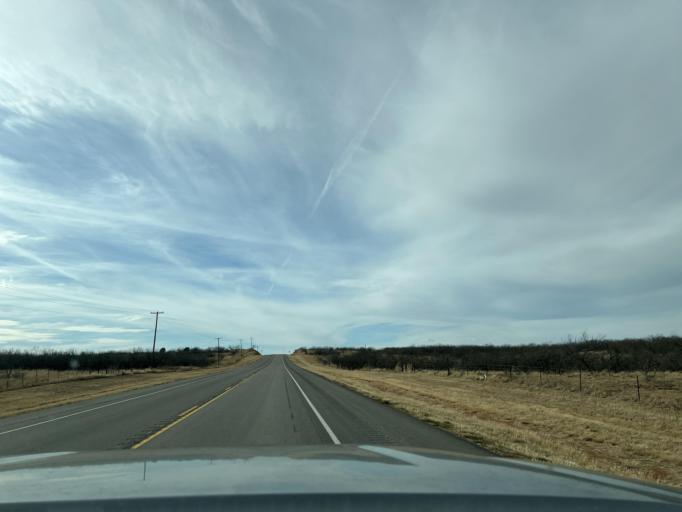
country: US
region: Texas
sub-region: Jones County
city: Anson
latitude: 32.7509
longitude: -99.7421
